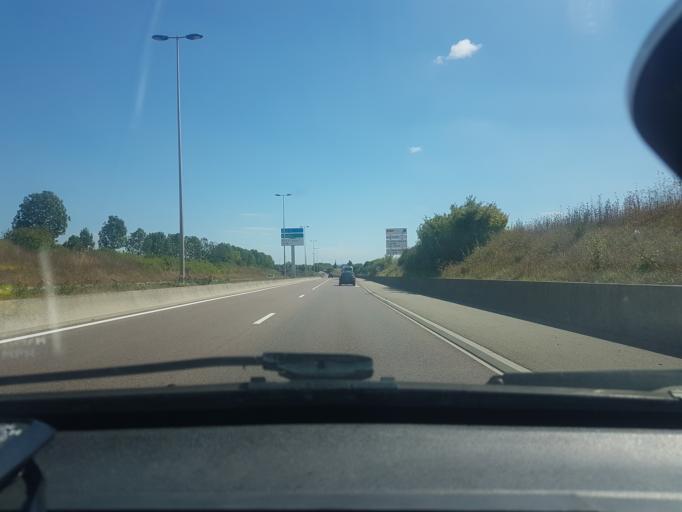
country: FR
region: Bourgogne
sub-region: Departement de la Cote-d'Or
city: Saint-Apollinaire
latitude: 47.3241
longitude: 5.0886
